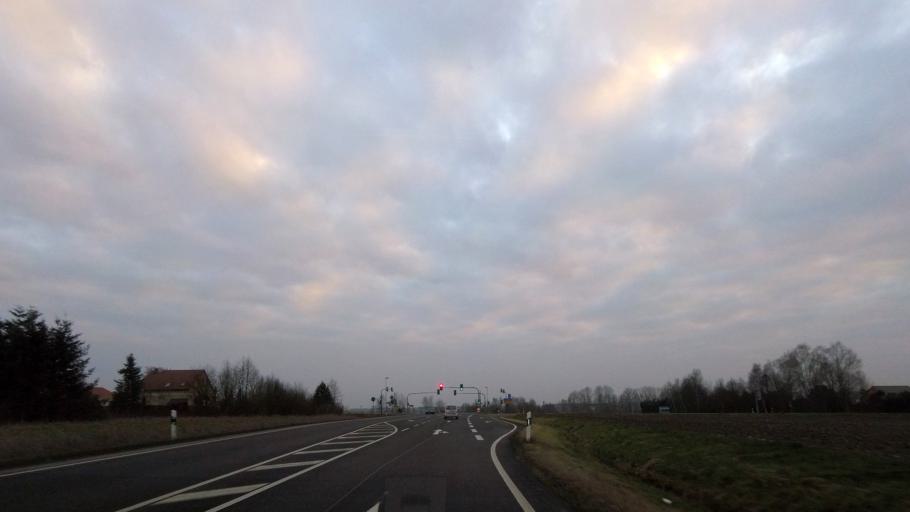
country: DE
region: Brandenburg
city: Beelitz
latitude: 52.2352
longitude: 12.9877
